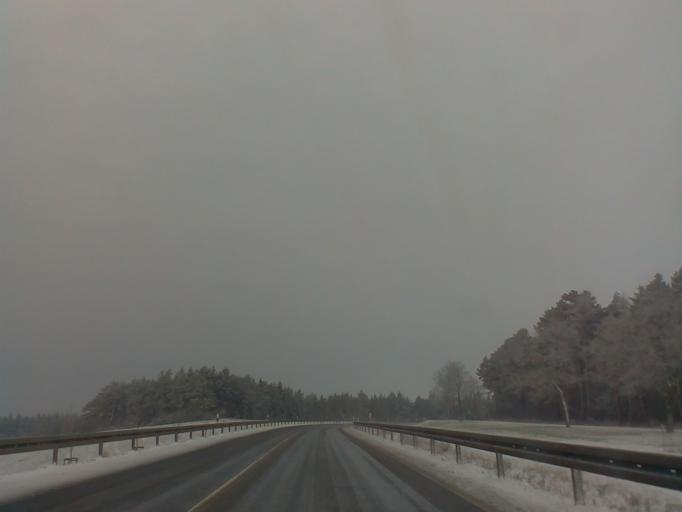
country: DE
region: Thuringia
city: Bad Blankenburg
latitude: 50.7291
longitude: 11.2287
